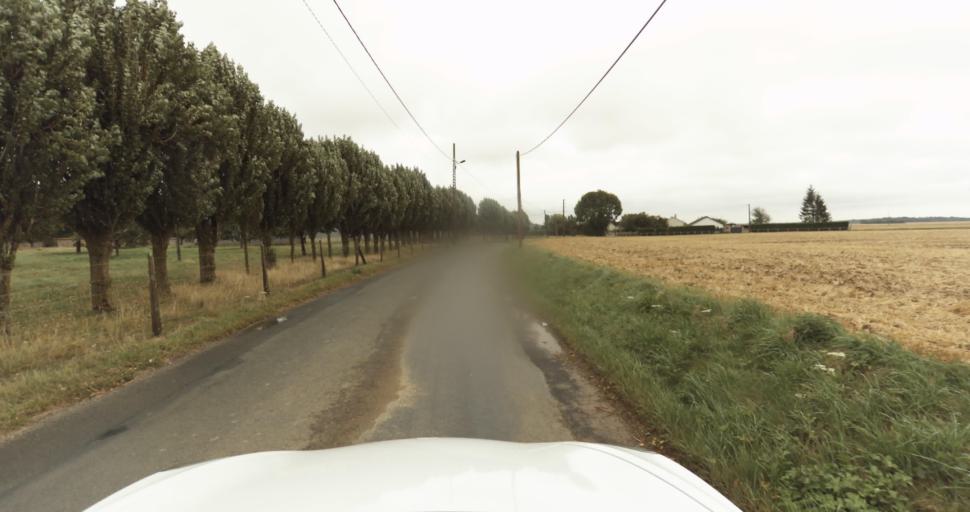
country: FR
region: Haute-Normandie
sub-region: Departement de l'Eure
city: Aviron
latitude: 49.0715
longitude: 1.0954
